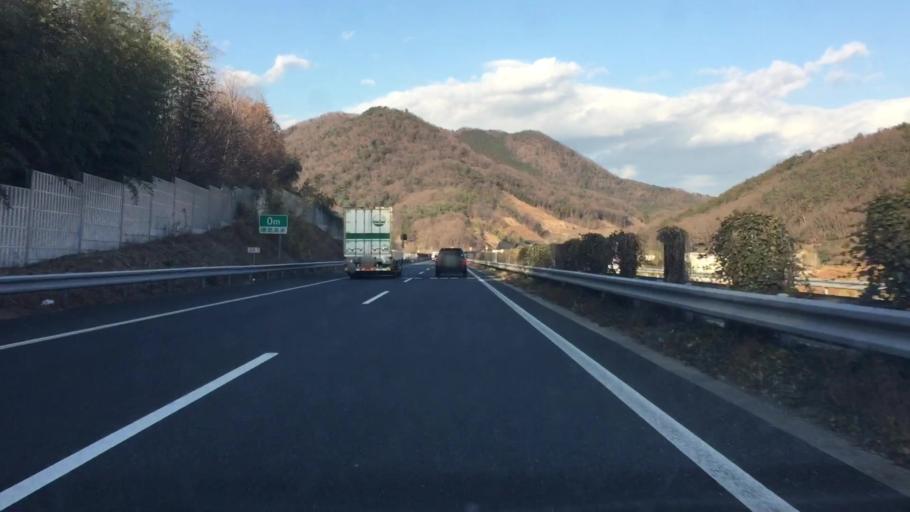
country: JP
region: Tochigi
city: Ashikaga
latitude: 36.3507
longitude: 139.4194
